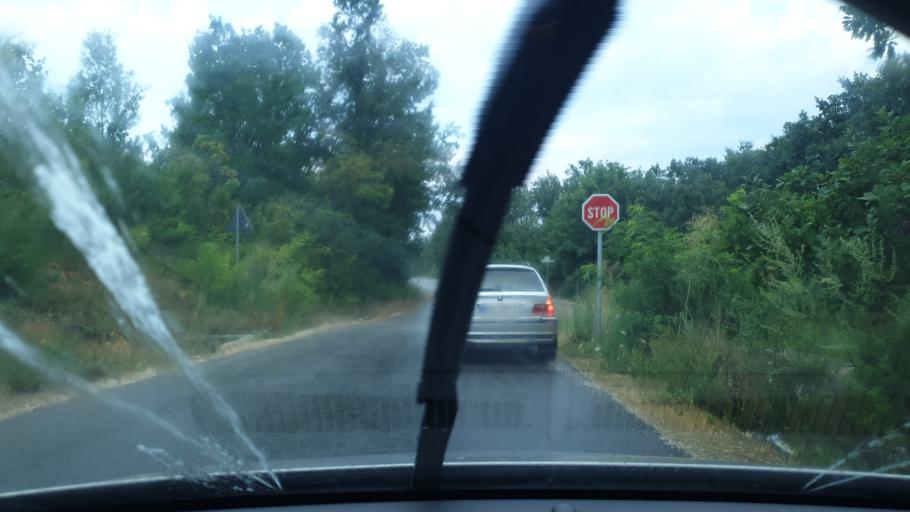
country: RS
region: Central Serbia
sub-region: Sumadijski Okrug
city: Kragujevac
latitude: 44.0518
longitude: 20.7827
